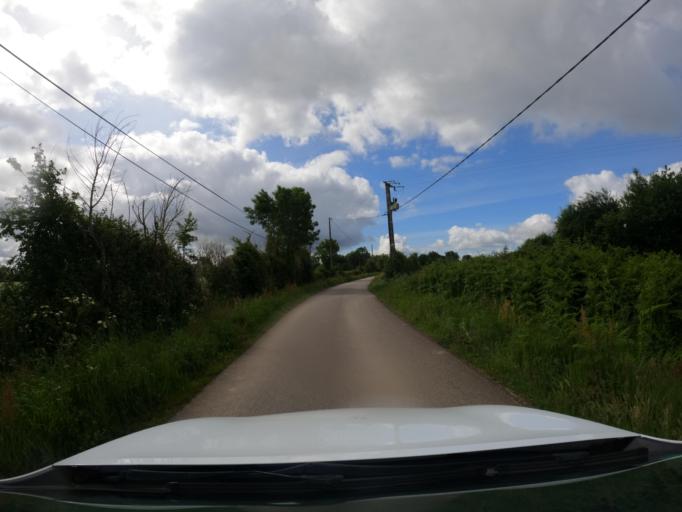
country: FR
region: Pays de la Loire
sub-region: Departement de la Vendee
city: Le Champ-Saint-Pere
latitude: 46.4918
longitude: -1.3571
